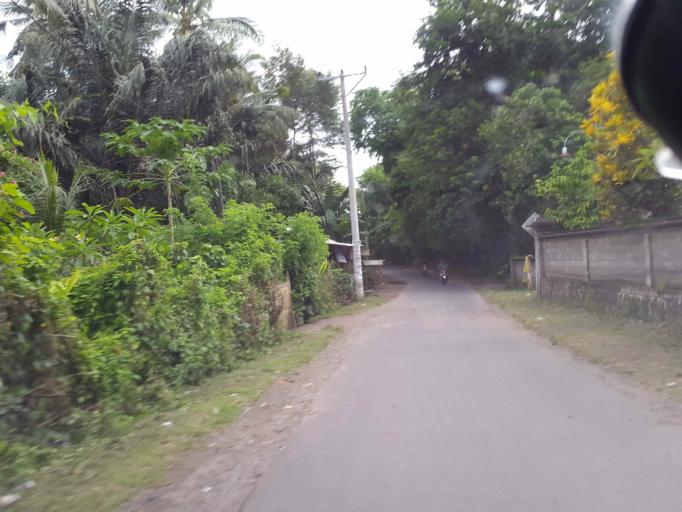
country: ID
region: West Nusa Tenggara
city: Mambalan
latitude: -8.5429
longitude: 116.1132
